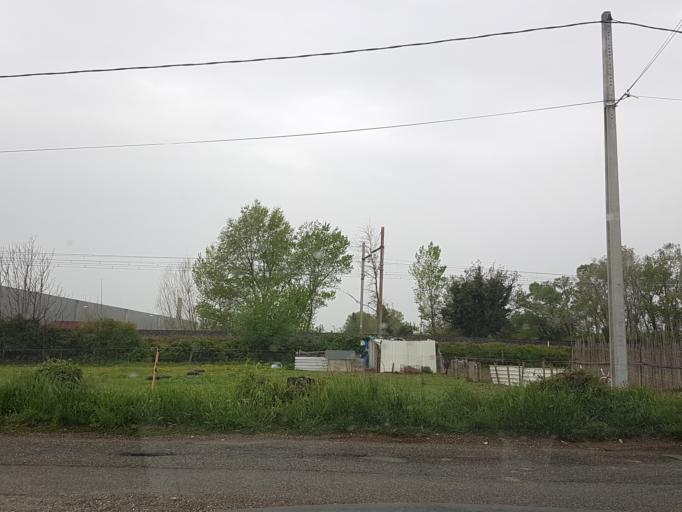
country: FR
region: Provence-Alpes-Cote d'Azur
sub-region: Departement du Vaucluse
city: Sorgues
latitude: 43.9872
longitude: 4.8684
